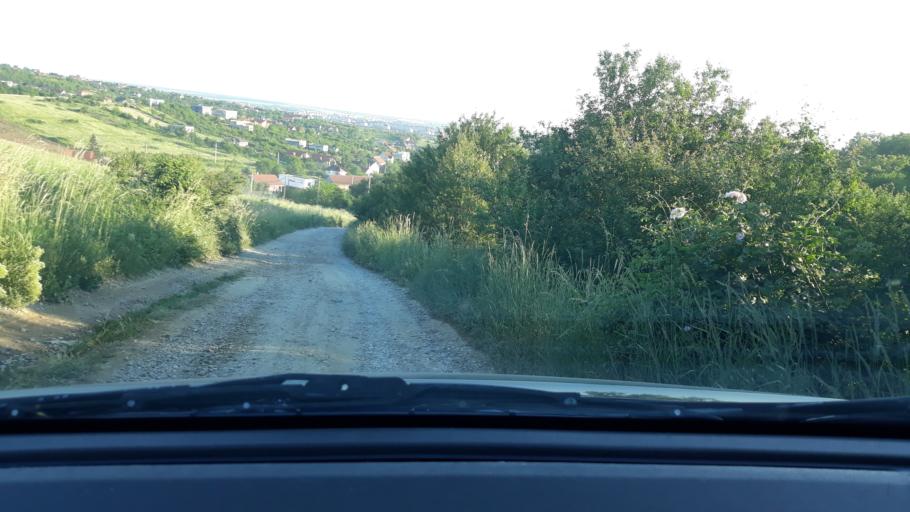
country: RO
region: Bihor
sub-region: Comuna Paleu
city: Paleu
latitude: 47.1015
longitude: 21.9353
